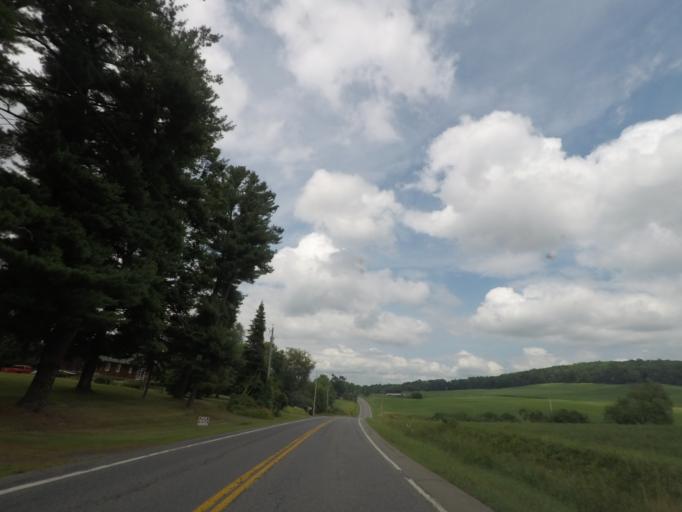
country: US
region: New York
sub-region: Saratoga County
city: Stillwater
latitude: 43.0361
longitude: -73.6839
